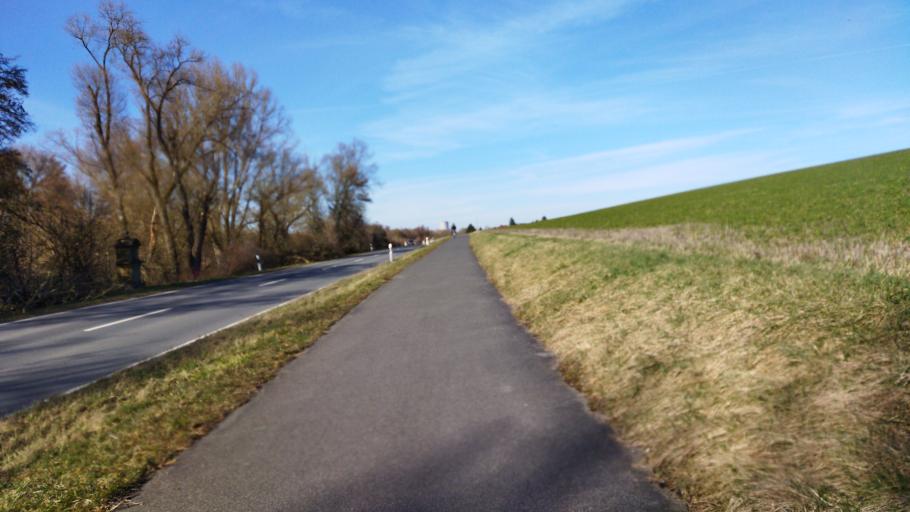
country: DE
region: Bavaria
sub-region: Regierungsbezirk Unterfranken
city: Wipfeld
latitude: 49.9346
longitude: 10.1825
